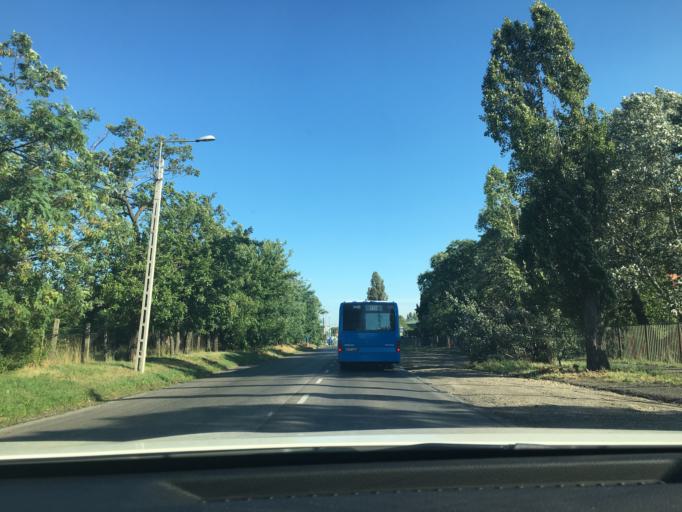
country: HU
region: Budapest
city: Budapest XVII. keruelet
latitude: 47.4963
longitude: 19.2400
